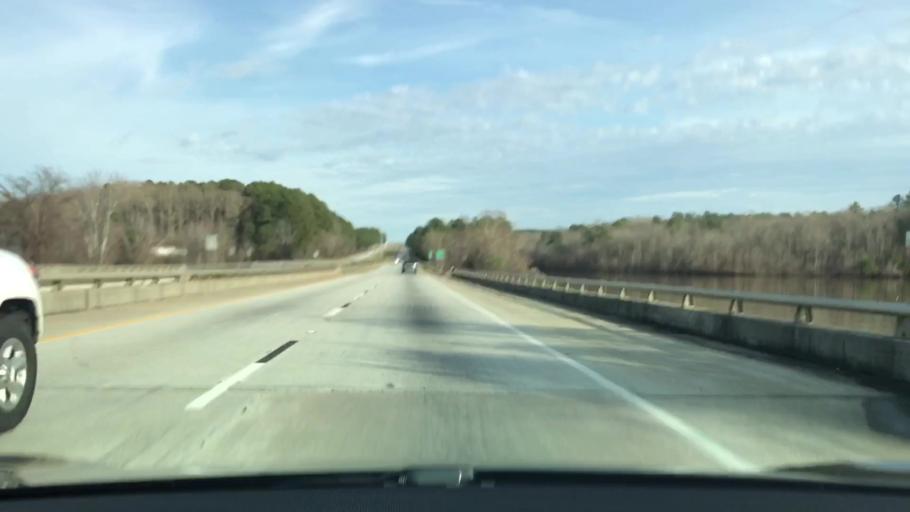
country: US
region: Georgia
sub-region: Putnam County
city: Jefferson
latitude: 33.5339
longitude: -83.2725
